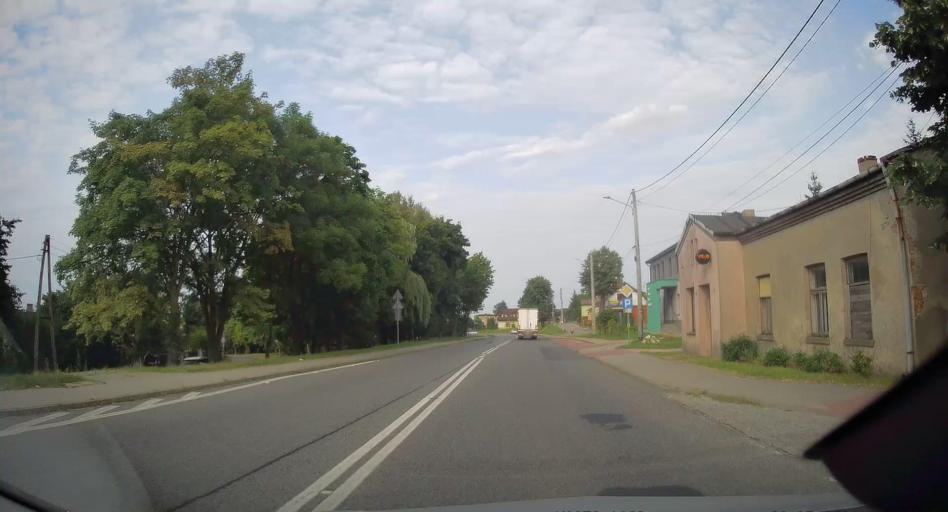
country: PL
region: Silesian Voivodeship
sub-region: Powiat czestochowski
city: Redziny
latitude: 50.8578
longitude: 19.2126
